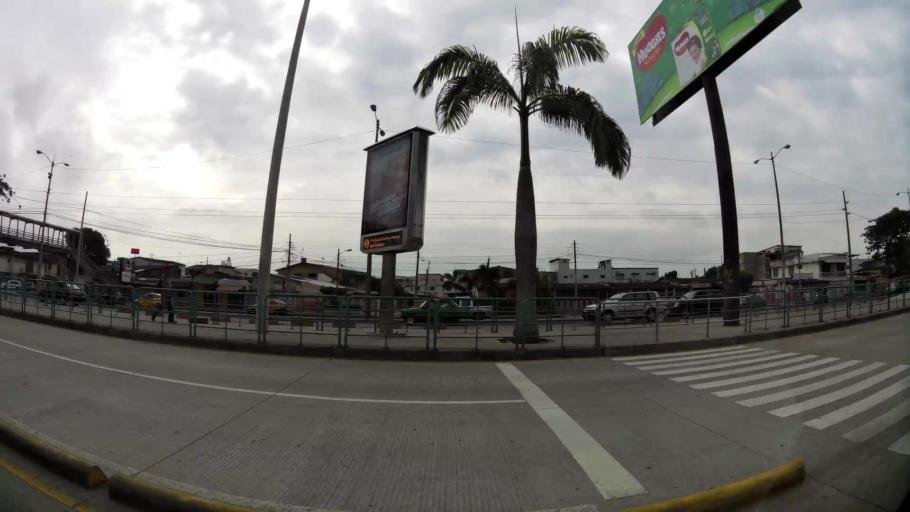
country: EC
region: Guayas
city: Guayaquil
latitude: -2.2268
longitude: -79.8982
